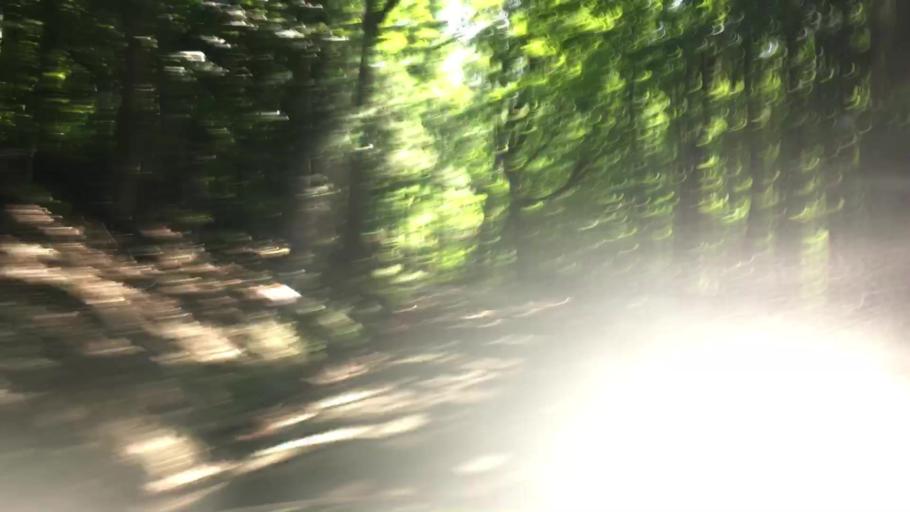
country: US
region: Vermont
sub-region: Windham County
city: West Brattleboro
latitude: 42.8018
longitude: -72.6532
